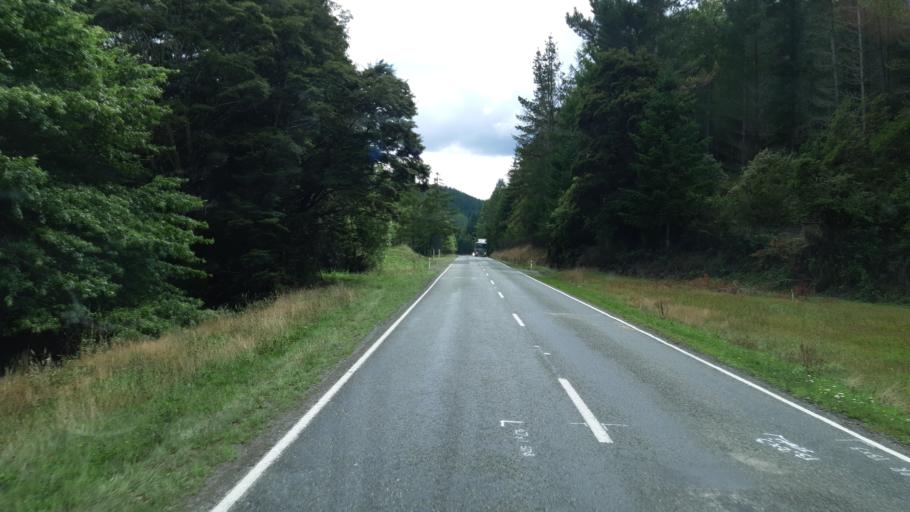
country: NZ
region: Tasman
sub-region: Tasman District
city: Wakefield
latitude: -41.6081
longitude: 172.7596
